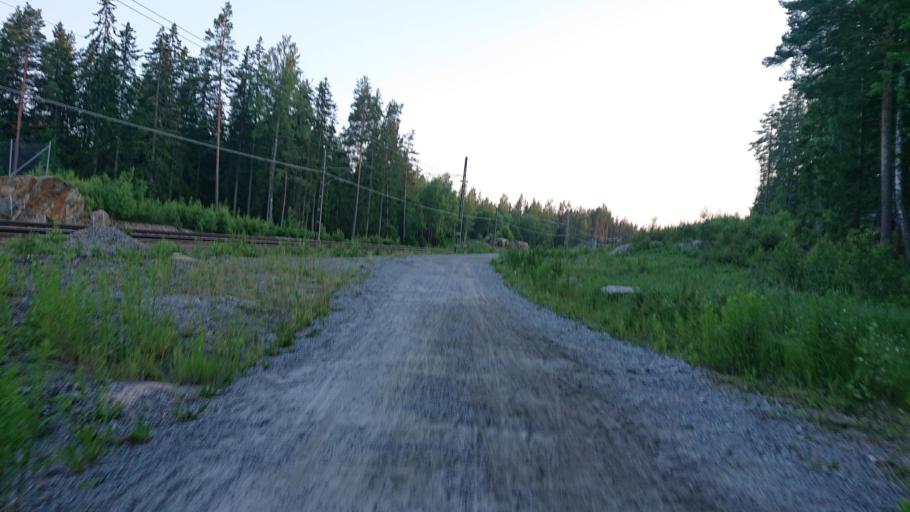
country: SE
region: Stockholm
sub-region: Osterakers Kommun
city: Akersberga
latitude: 59.4705
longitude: 18.2290
